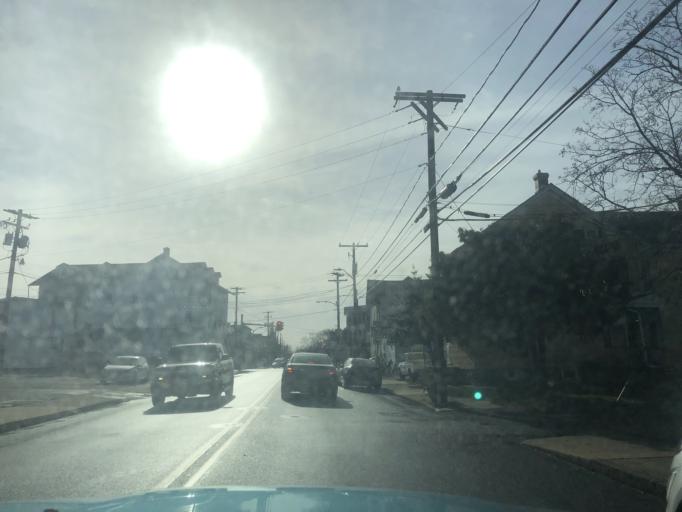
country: US
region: Pennsylvania
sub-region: Bucks County
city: Quakertown
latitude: 40.4422
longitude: -75.3331
